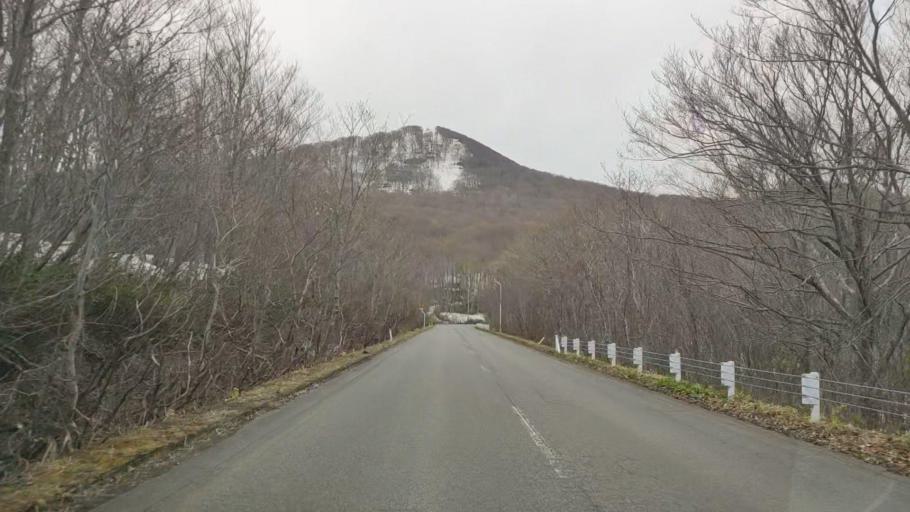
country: JP
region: Aomori
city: Aomori Shi
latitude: 40.6556
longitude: 140.9551
